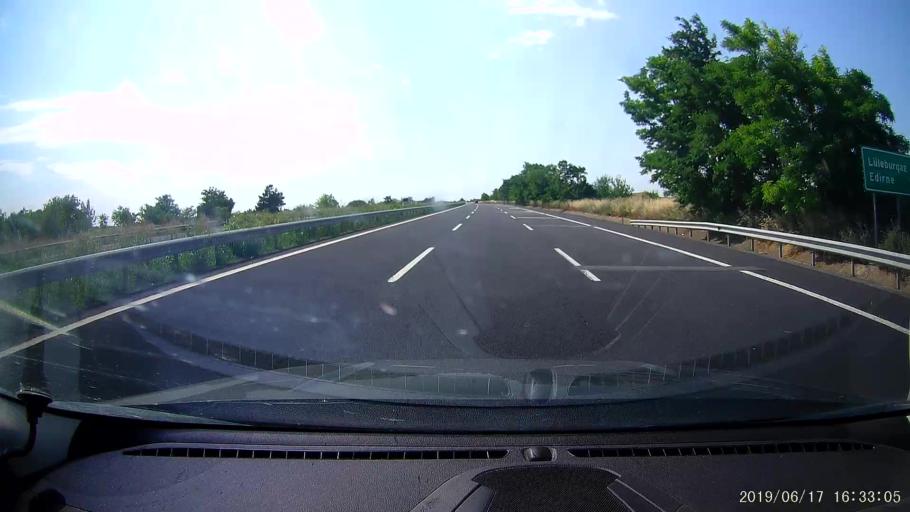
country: TR
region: Kirklareli
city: Buyukkaristiran
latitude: 41.3776
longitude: 27.5839
